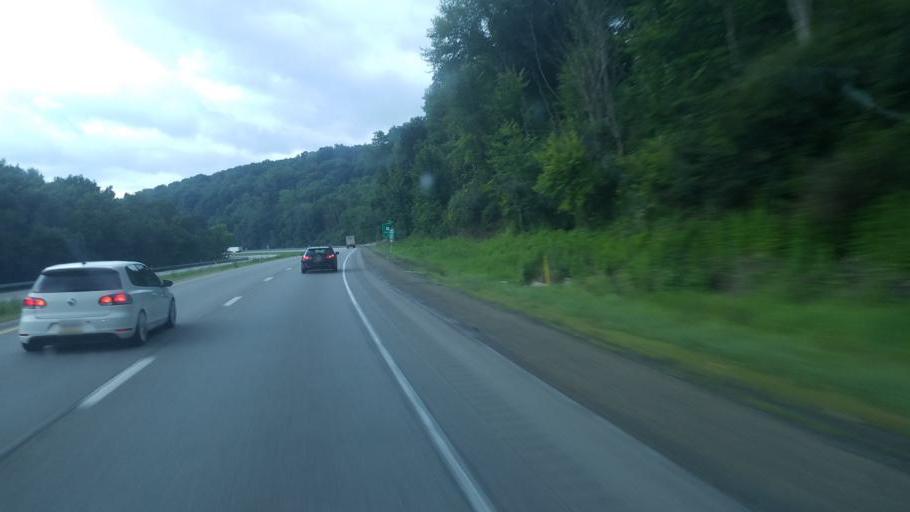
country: US
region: Pennsylvania
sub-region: Butler County
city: Zelienople
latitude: 40.8399
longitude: -80.1032
